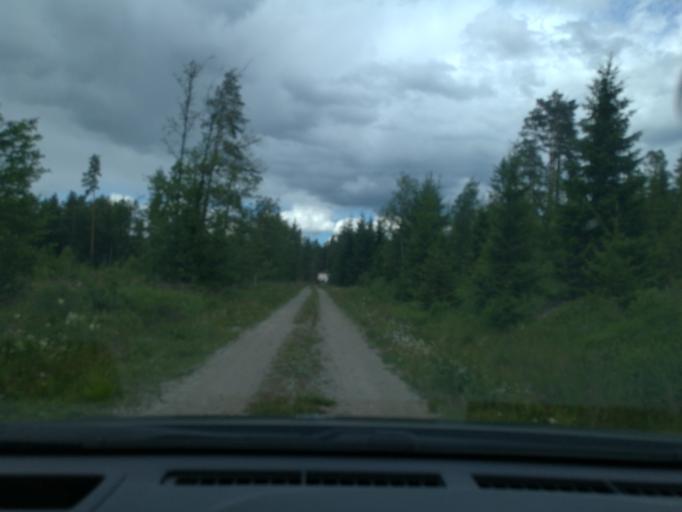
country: SE
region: Vaestmanland
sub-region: Vasteras
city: Skultuna
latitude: 59.8009
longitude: 16.3300
